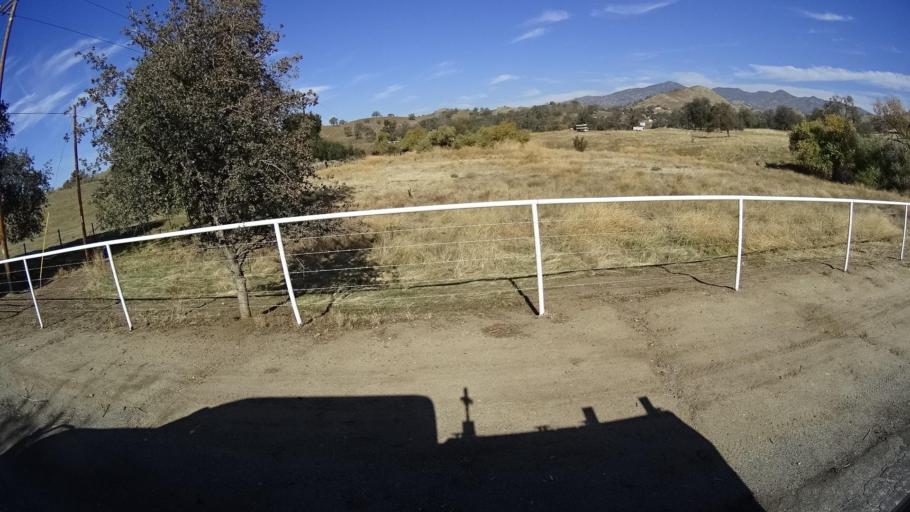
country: US
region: California
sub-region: Tulare County
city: Richgrove
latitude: 35.6990
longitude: -118.8410
